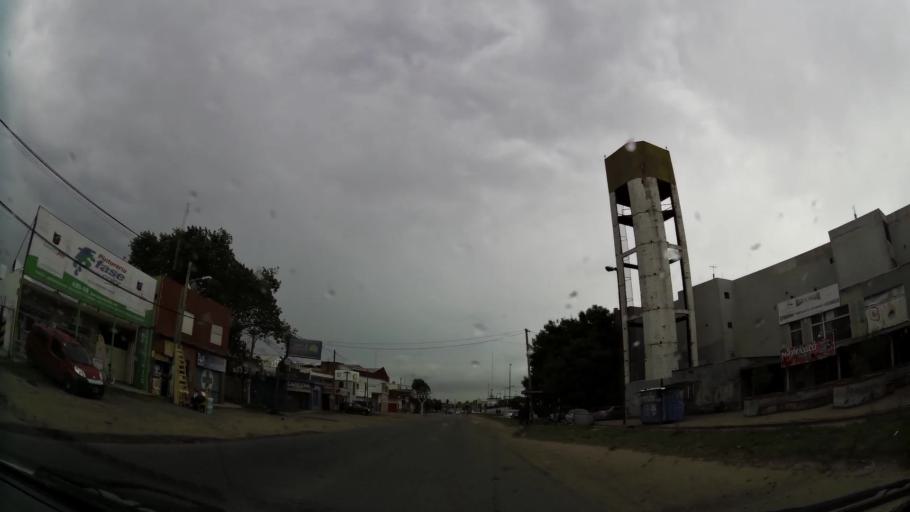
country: AR
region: Buenos Aires
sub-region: Partido de Quilmes
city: Quilmes
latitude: -34.7871
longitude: -58.2509
